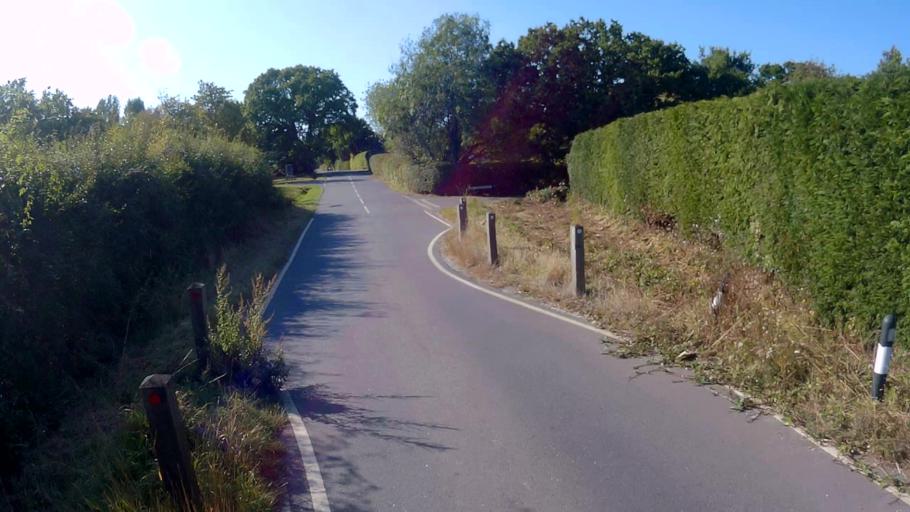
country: GB
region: England
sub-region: Hampshire
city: Lindford
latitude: 51.1587
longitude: -0.8203
